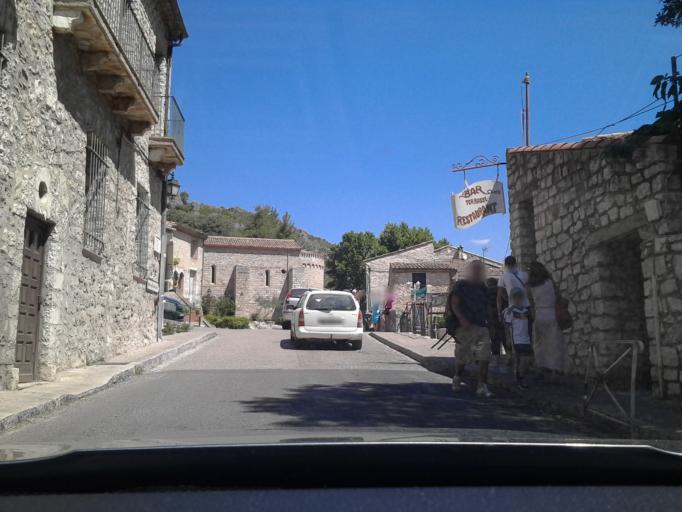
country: FR
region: Languedoc-Roussillon
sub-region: Departement de l'Herault
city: Saint-Jean-de-Fos
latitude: 43.7327
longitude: 3.5537
